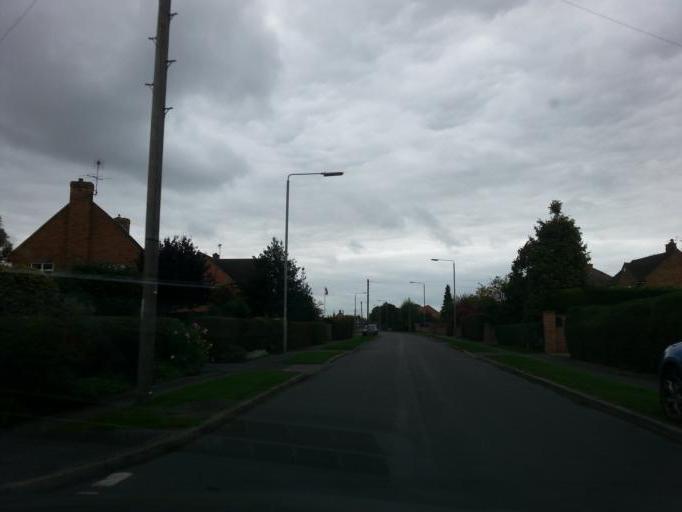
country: GB
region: England
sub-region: Nottinghamshire
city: Newark on Trent
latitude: 53.0584
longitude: -0.7764
